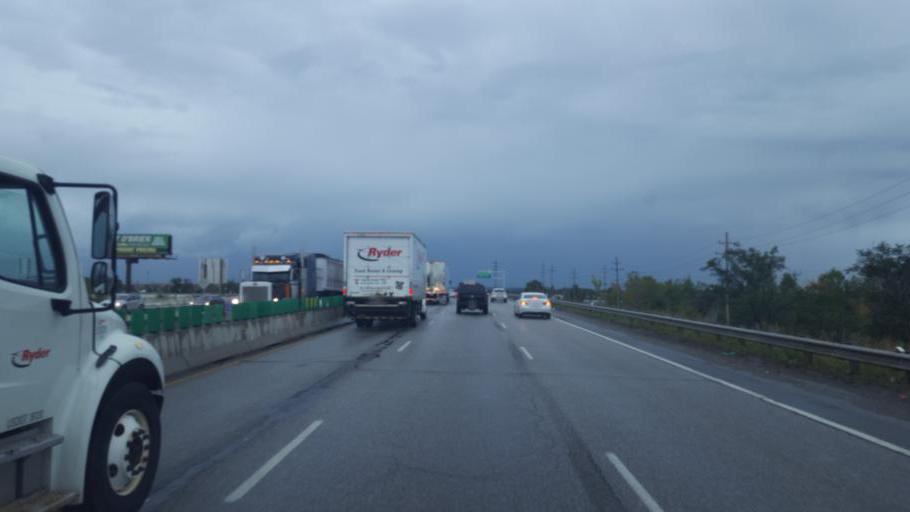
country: US
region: Ohio
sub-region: Cuyahoga County
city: Bedford Heights
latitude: 41.4171
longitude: -81.5086
